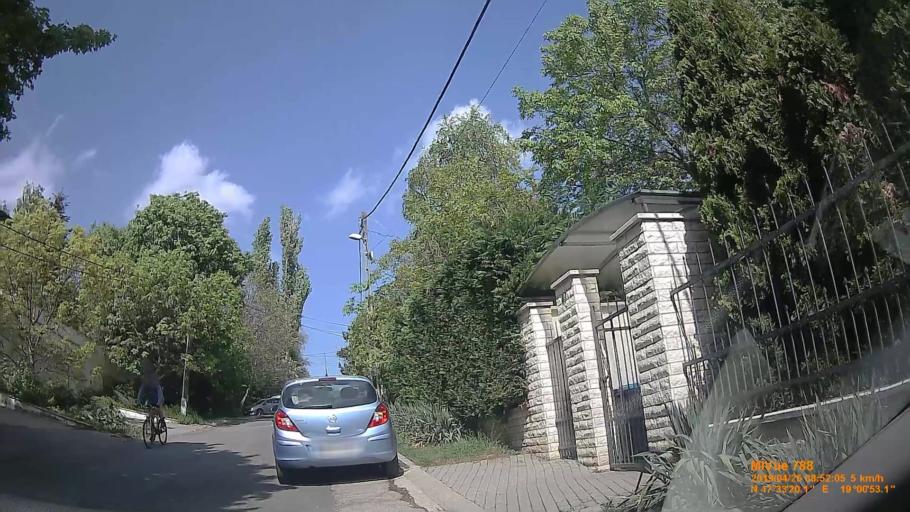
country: HU
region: Budapest
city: Budapest III. keruelet
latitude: 47.5556
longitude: 19.0147
